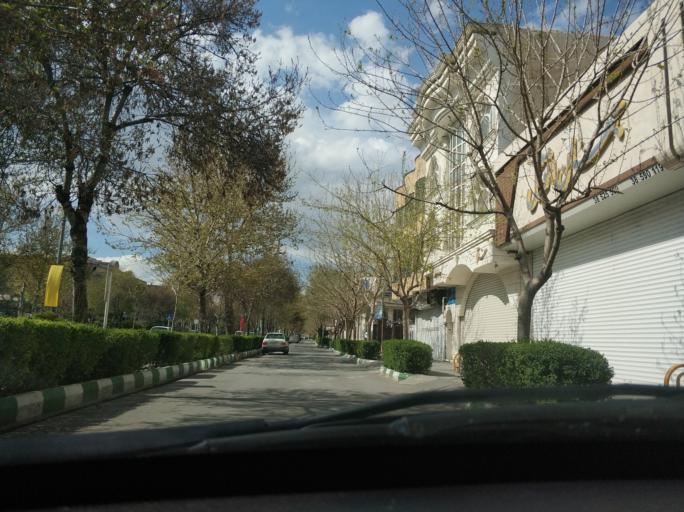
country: IR
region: Razavi Khorasan
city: Mashhad
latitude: 36.2710
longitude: 59.5960
